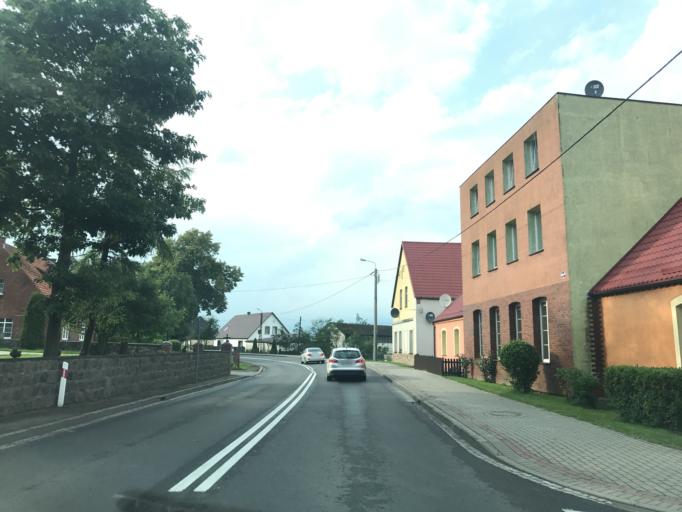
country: PL
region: Pomeranian Voivodeship
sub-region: Powiat czluchowski
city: Przechlewo
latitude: 53.7367
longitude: 17.1927
